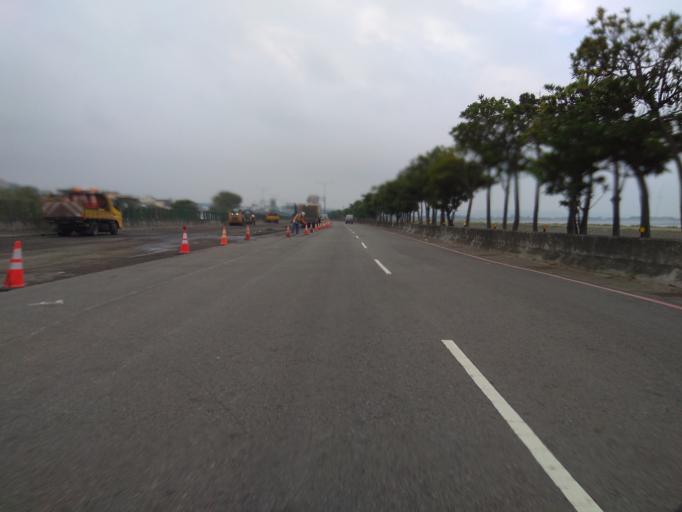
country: TW
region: Taiwan
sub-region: Hsinchu
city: Hsinchu
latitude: 24.7761
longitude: 120.9142
